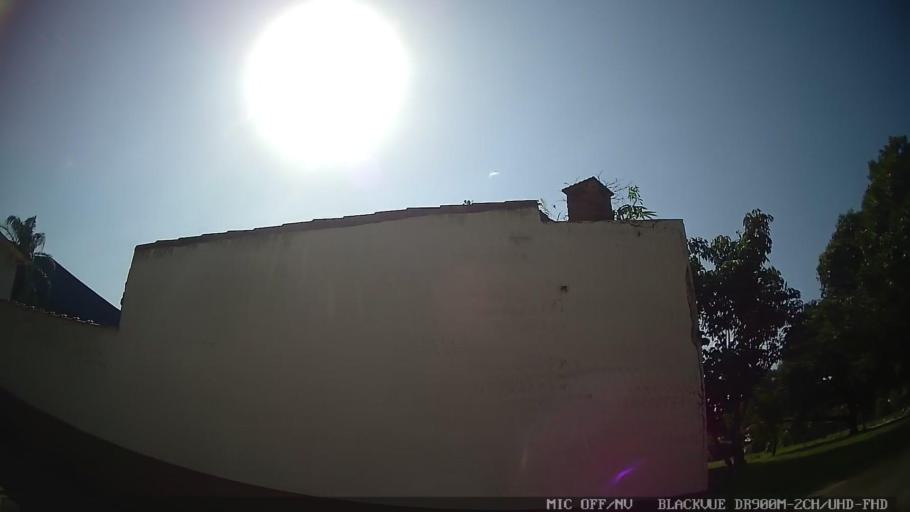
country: BR
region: Sao Paulo
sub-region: Guaruja
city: Guaruja
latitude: -23.9704
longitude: -46.1901
